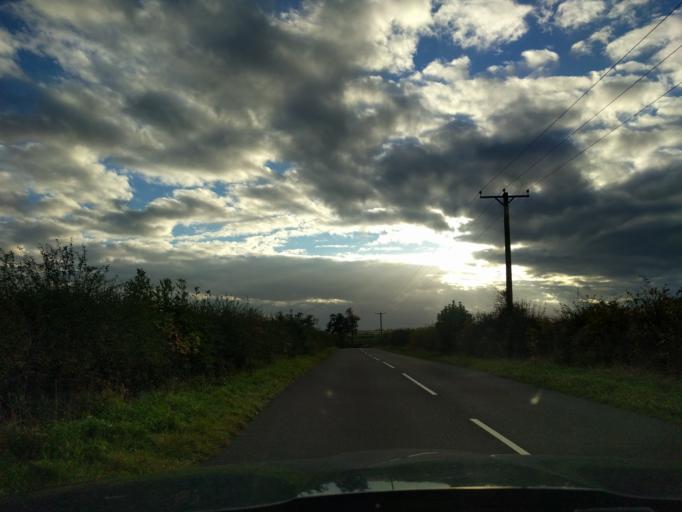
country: GB
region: England
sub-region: Northumberland
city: Ford
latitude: 55.7314
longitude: -2.1039
